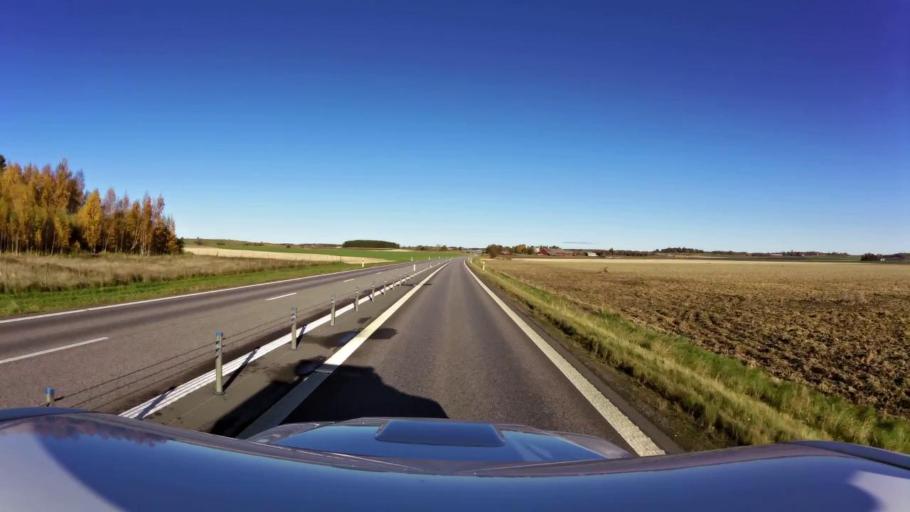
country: SE
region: OEstergoetland
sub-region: Linkopings Kommun
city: Berg
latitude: 58.4600
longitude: 15.4982
